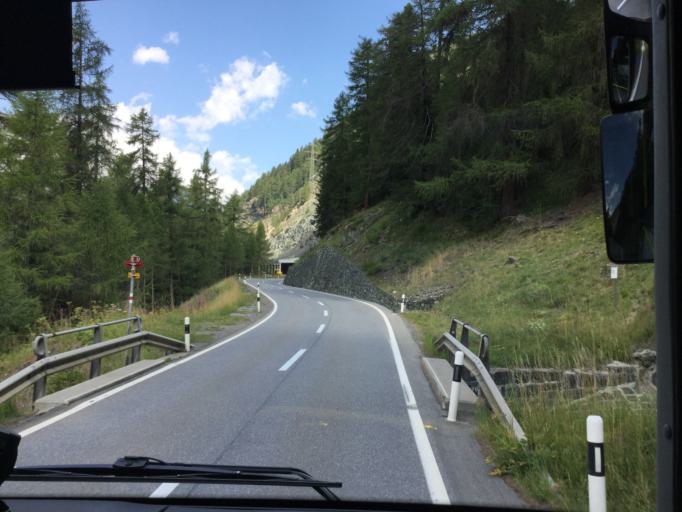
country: CH
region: Grisons
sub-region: Maloja District
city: Silvaplana
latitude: 46.5039
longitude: 9.6409
